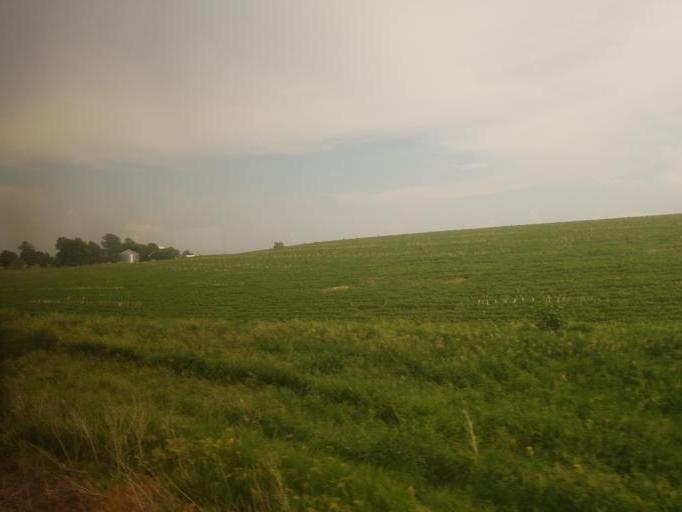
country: US
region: Illinois
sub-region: Henry County
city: Kewanee
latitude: 41.3039
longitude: -89.7560
